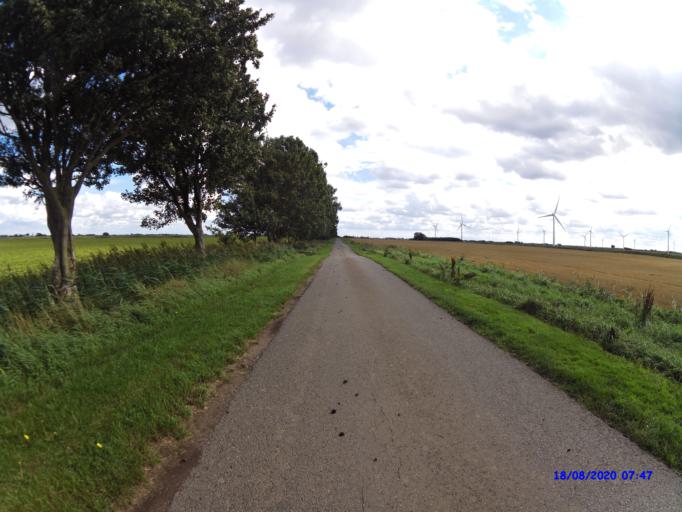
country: GB
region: England
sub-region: Cambridgeshire
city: Whittlesey
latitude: 52.5236
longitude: -0.0989
